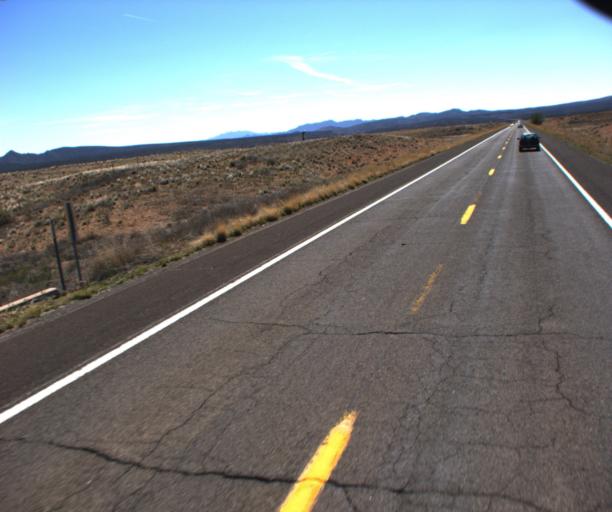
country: US
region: Arizona
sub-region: Mohave County
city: Peach Springs
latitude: 35.4759
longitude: -113.5820
